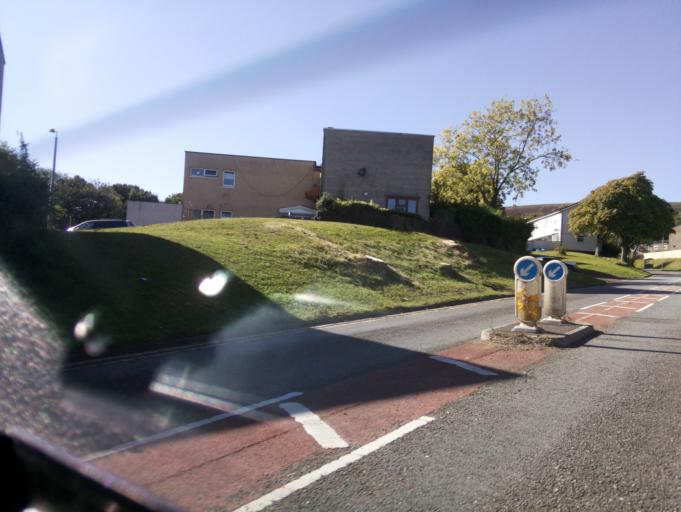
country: GB
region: Wales
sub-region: Torfaen County Borough
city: Cwmbran
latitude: 51.6518
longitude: -3.0455
